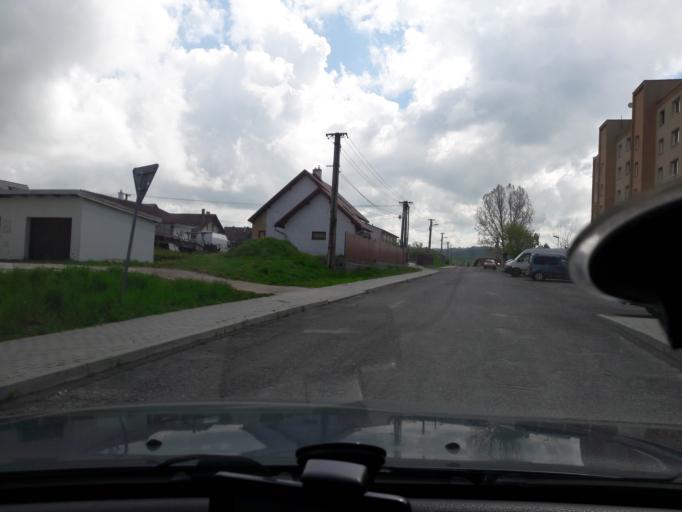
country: SK
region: Banskobystricky
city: Krupina
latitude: 48.4281
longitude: 19.1492
